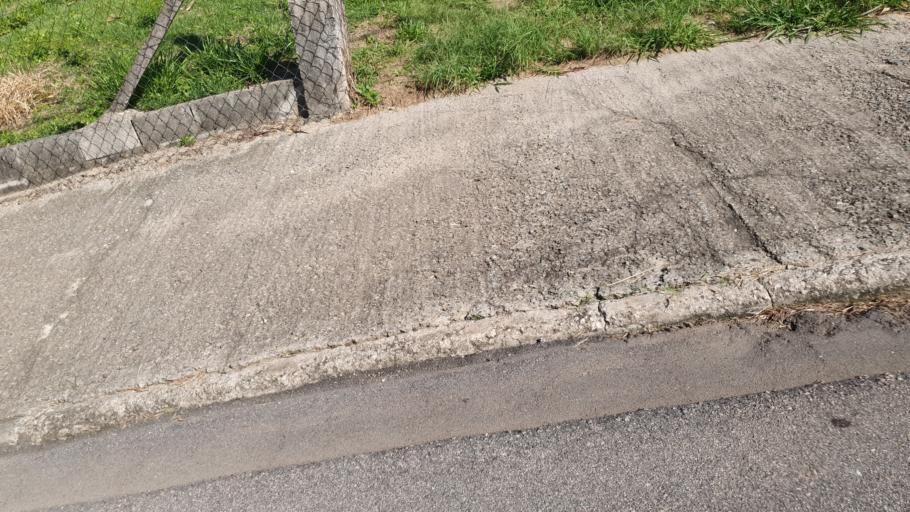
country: BR
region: Sao Paulo
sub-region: Sorocaba
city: Sorocaba
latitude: -23.4991
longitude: -47.4768
